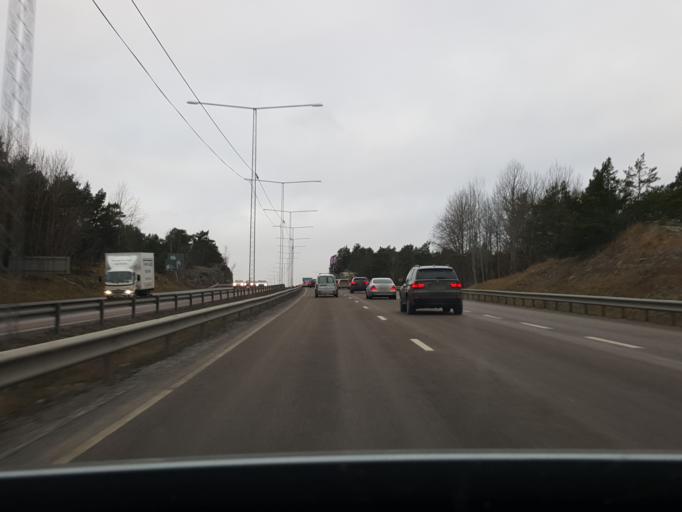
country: SE
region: Stockholm
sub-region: Nacka Kommun
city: Nacka
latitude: 59.3160
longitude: 18.1965
